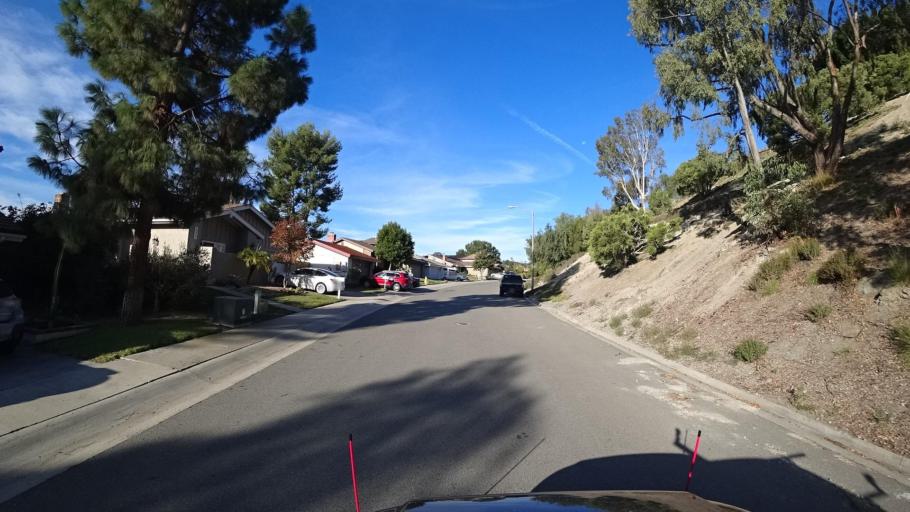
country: US
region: California
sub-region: San Diego County
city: Spring Valley
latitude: 32.7359
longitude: -116.9779
